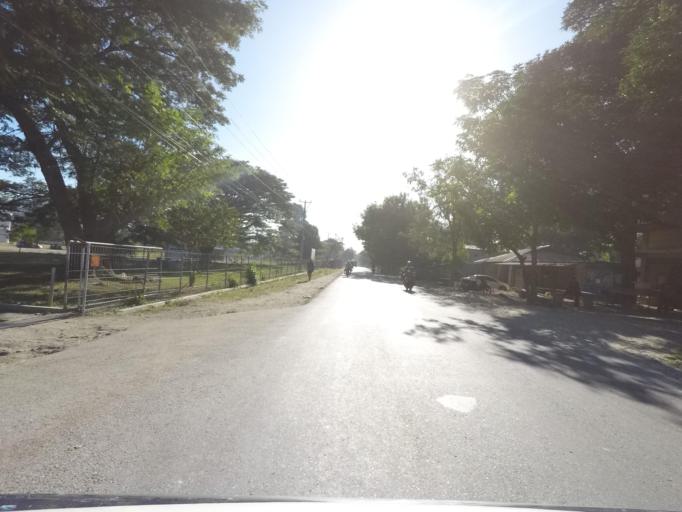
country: ID
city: Metinaro
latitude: -8.5522
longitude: 125.6605
